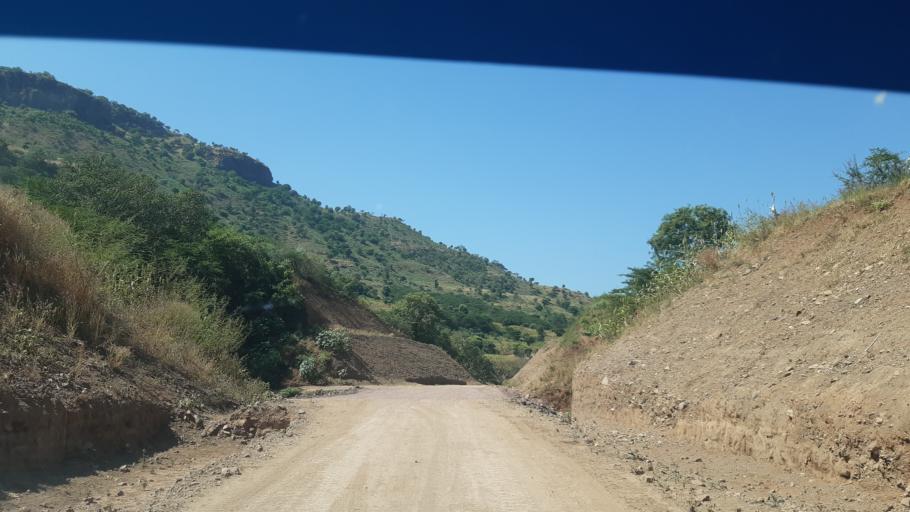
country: ET
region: Amhara
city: Dabat
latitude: 13.1931
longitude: 37.5742
